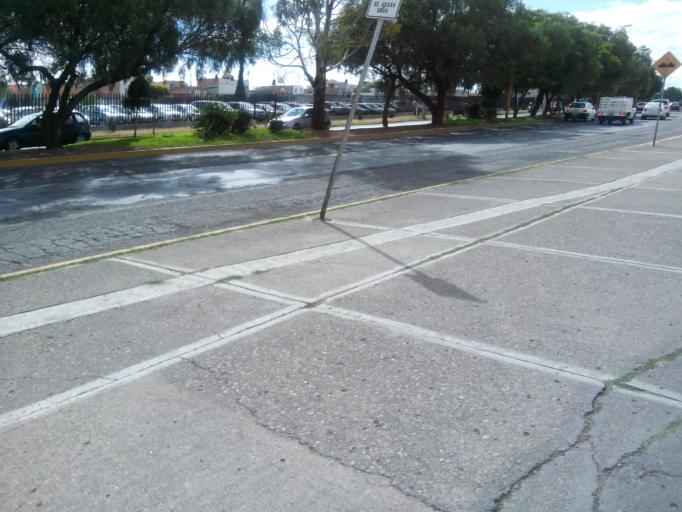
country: MX
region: Aguascalientes
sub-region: Aguascalientes
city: Aguascalientes
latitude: 21.8583
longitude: -102.2832
